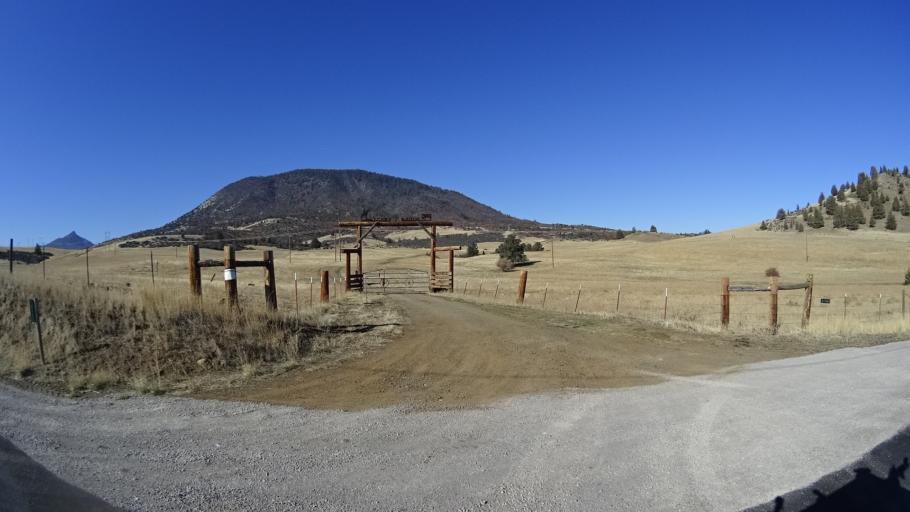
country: US
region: California
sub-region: Siskiyou County
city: Montague
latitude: 41.8575
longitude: -122.4650
